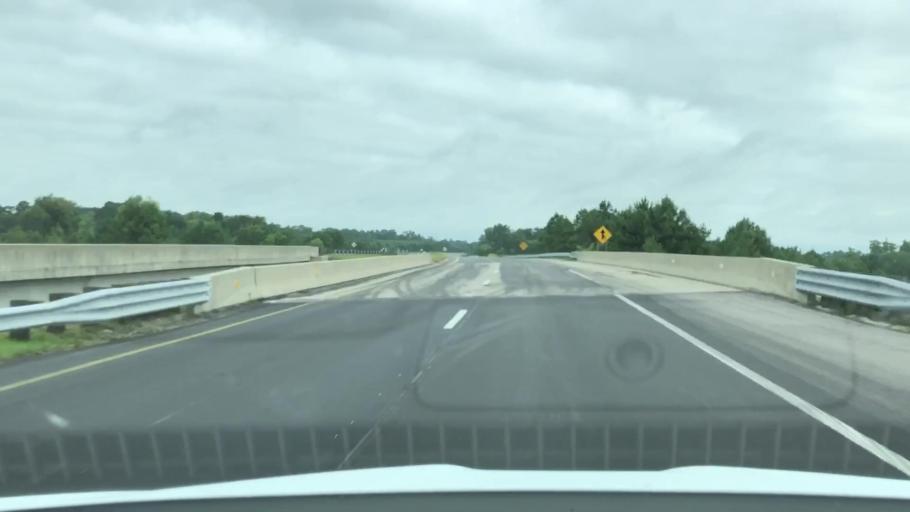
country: US
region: North Carolina
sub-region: Wilson County
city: Lucama
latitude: 35.6668
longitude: -77.9563
